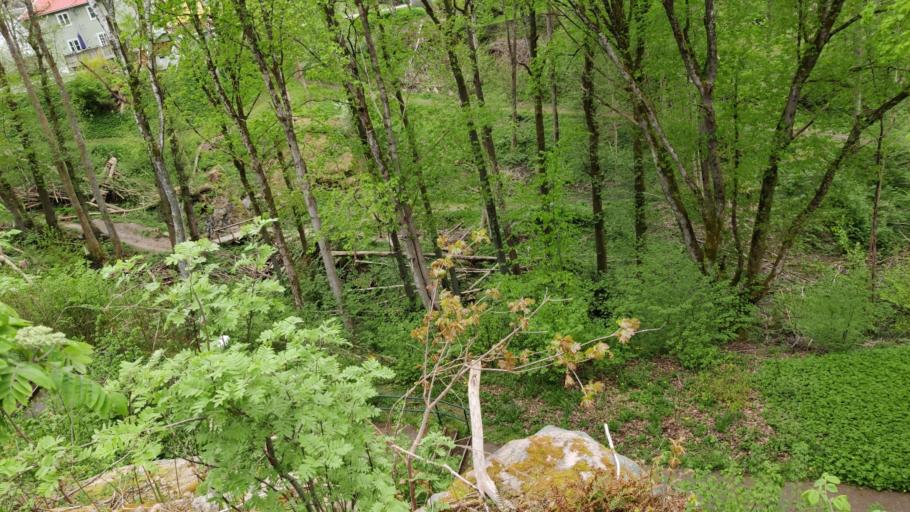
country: SE
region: Vaestra Goetaland
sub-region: Uddevalla Kommun
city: Uddevalla
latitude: 58.3388
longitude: 11.9309
